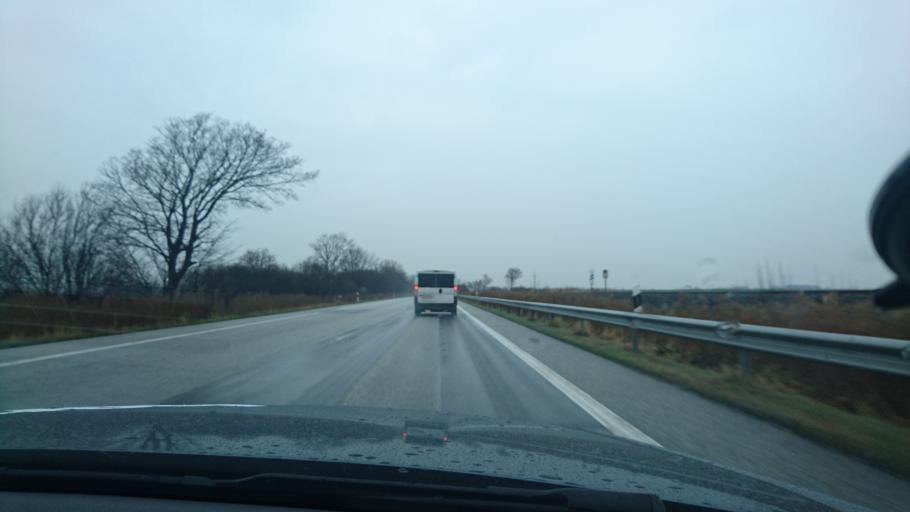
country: DE
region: Schleswig-Holstein
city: Fehmarn
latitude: 54.4388
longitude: 11.1569
